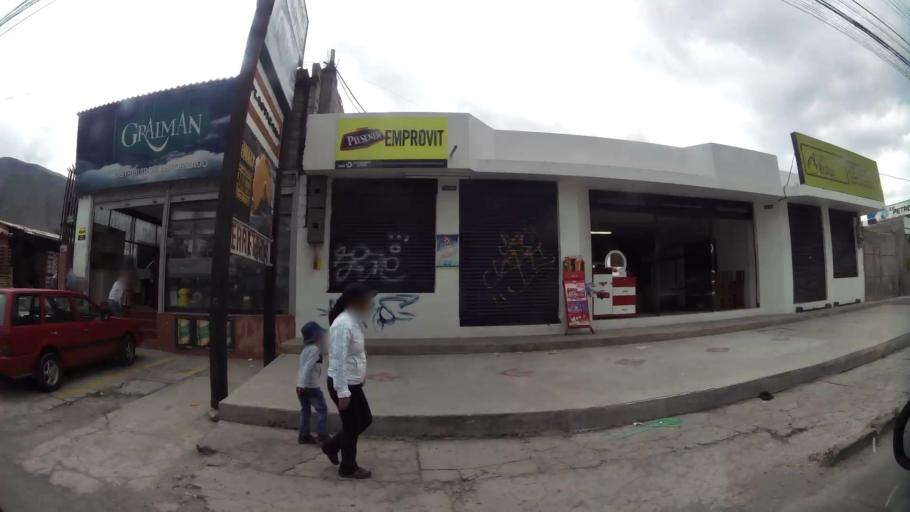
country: EC
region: Pichincha
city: Quito
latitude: -0.0104
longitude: -78.4467
